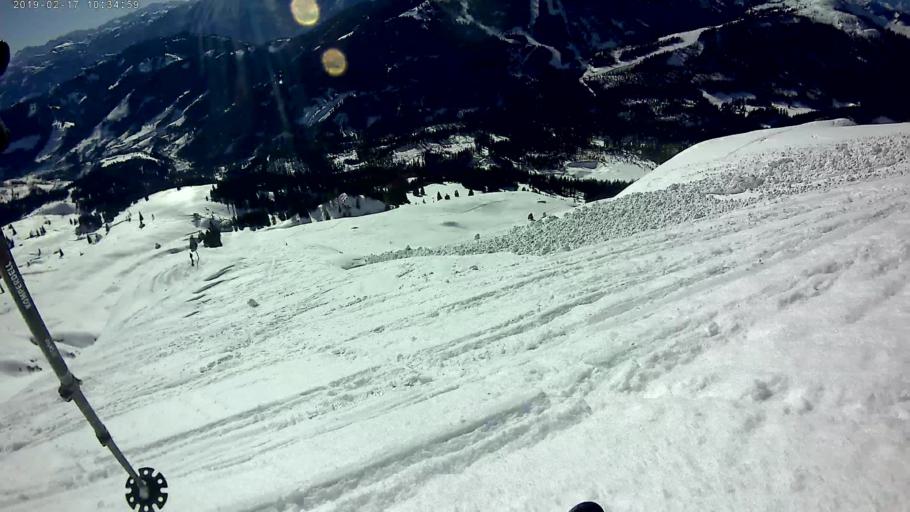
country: AT
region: Salzburg
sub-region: Politischer Bezirk Sankt Johann im Pongau
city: Muhlbach am Hochkonig
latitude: 47.4090
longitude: 13.0797
